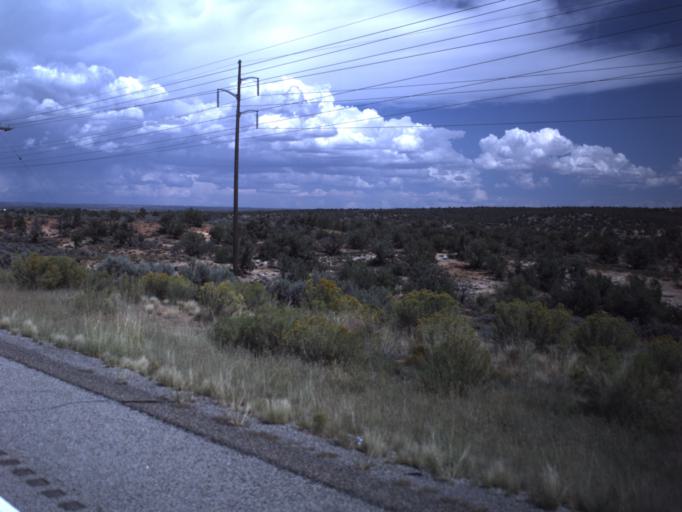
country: US
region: Utah
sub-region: San Juan County
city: Blanding
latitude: 37.5336
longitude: -109.4941
